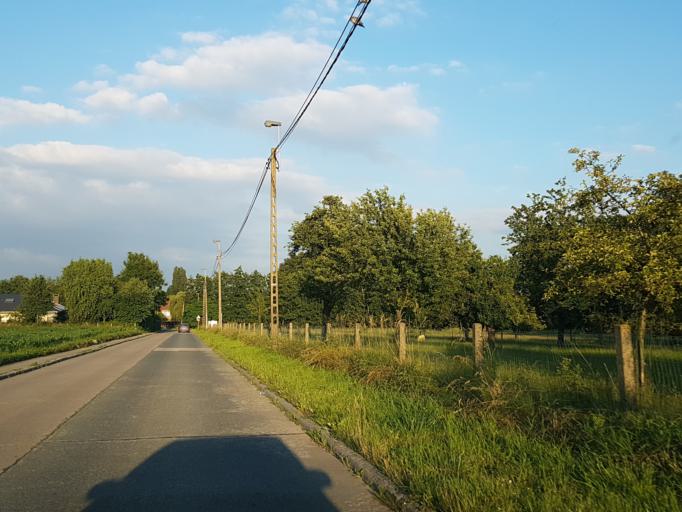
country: BE
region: Flanders
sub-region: Provincie Vlaams-Brabant
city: Ternat
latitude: 50.8636
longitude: 4.1926
